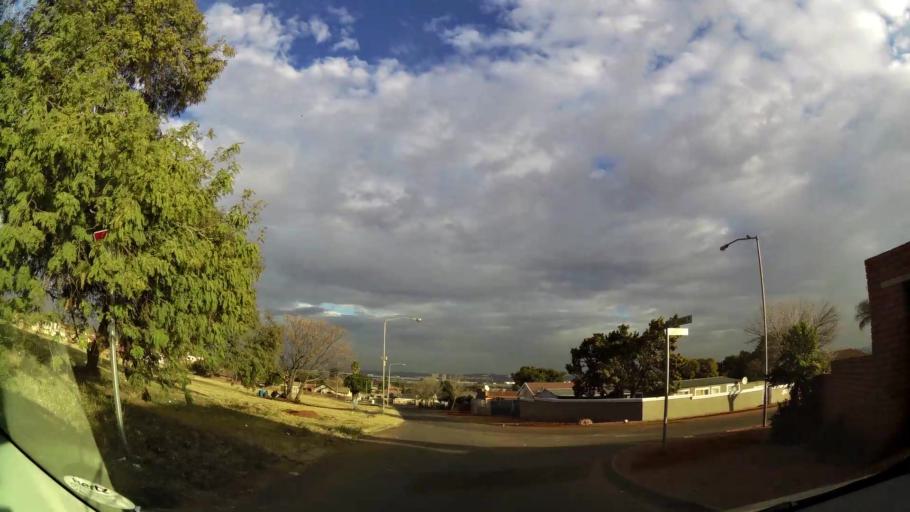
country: ZA
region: Gauteng
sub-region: City of Tshwane Metropolitan Municipality
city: Pretoria
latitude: -25.7016
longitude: 28.3190
